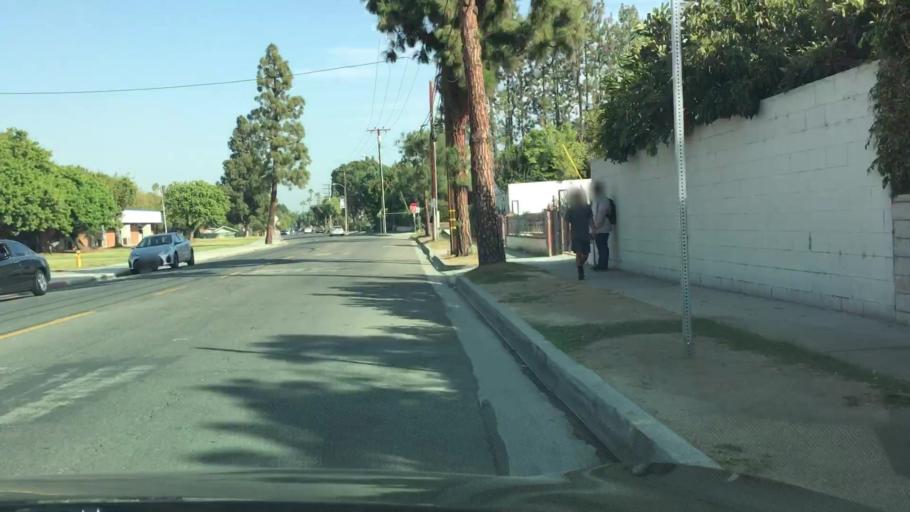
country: US
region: California
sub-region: Los Angeles County
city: Hacienda Heights
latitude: 34.0071
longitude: -117.9773
